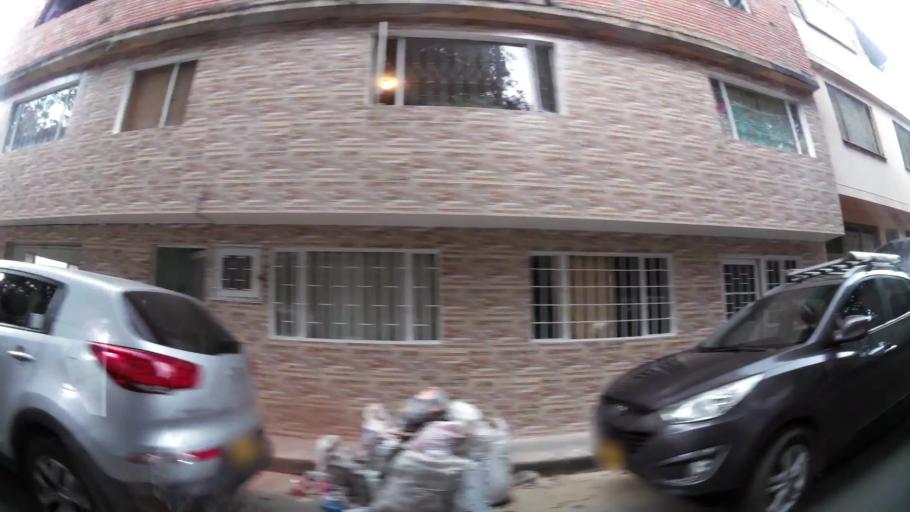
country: CO
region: Cundinamarca
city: La Calera
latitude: 4.7425
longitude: -74.0337
